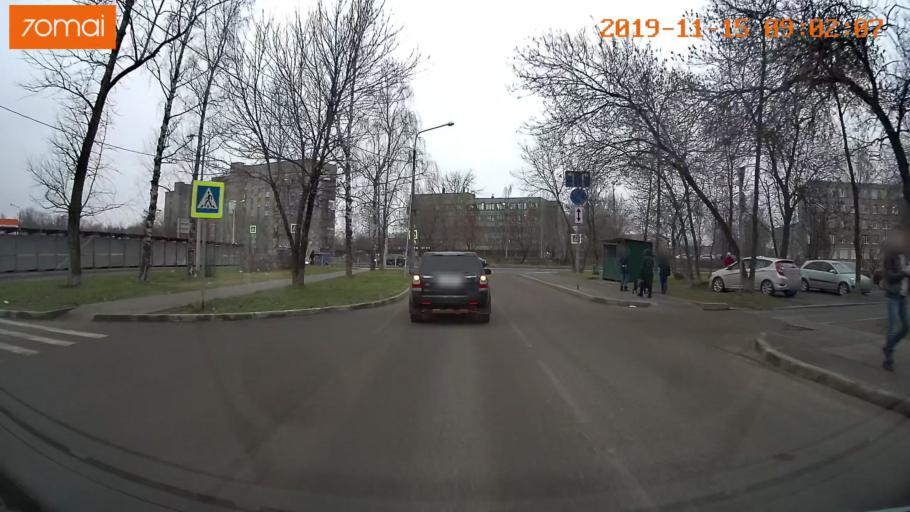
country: RU
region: Vologda
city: Cherepovets
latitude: 59.1358
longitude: 37.9269
